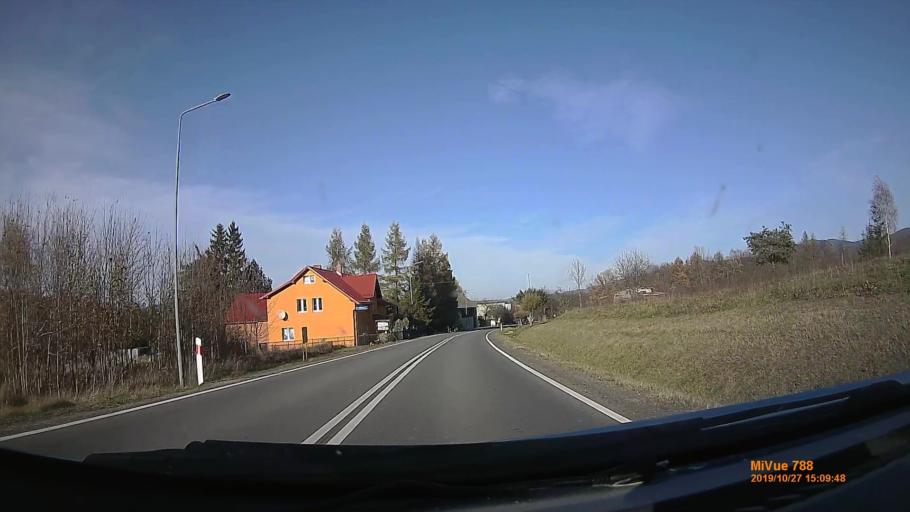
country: PL
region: Lower Silesian Voivodeship
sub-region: Powiat klodzki
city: Miedzylesie
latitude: 50.1828
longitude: 16.6683
